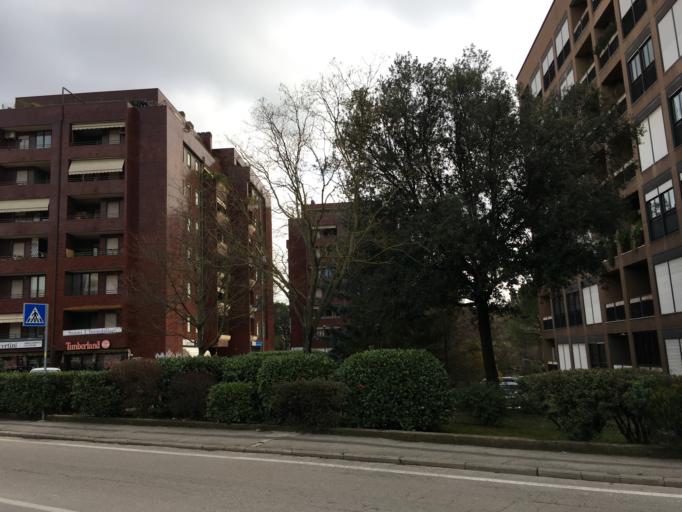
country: IT
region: Umbria
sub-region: Provincia di Perugia
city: Perugia
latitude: 43.1024
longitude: 12.3691
